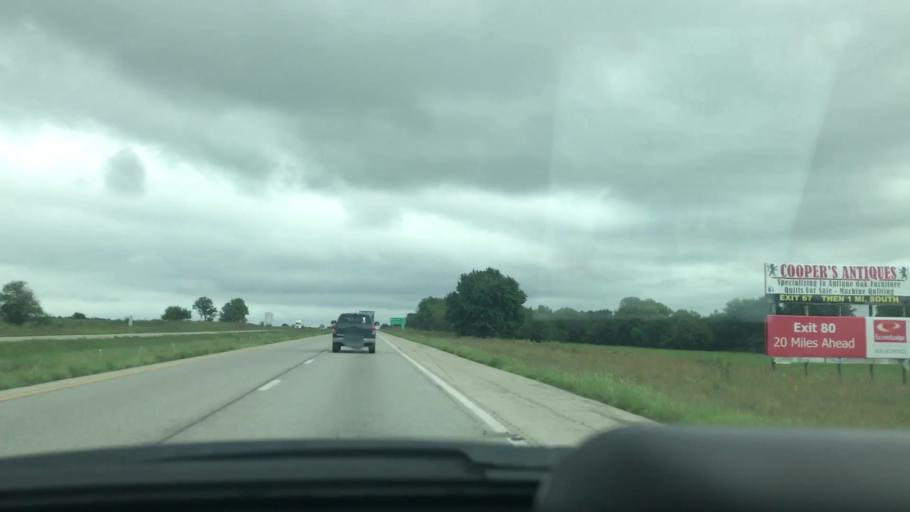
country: US
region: Missouri
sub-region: Greene County
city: Ash Grove
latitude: 37.1871
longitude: -93.6209
